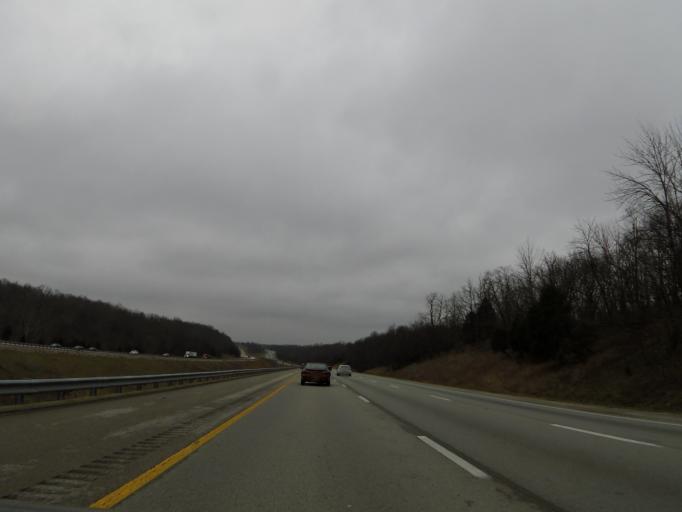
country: US
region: Kentucky
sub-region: Grant County
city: Williamstown
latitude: 38.4295
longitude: -84.5748
